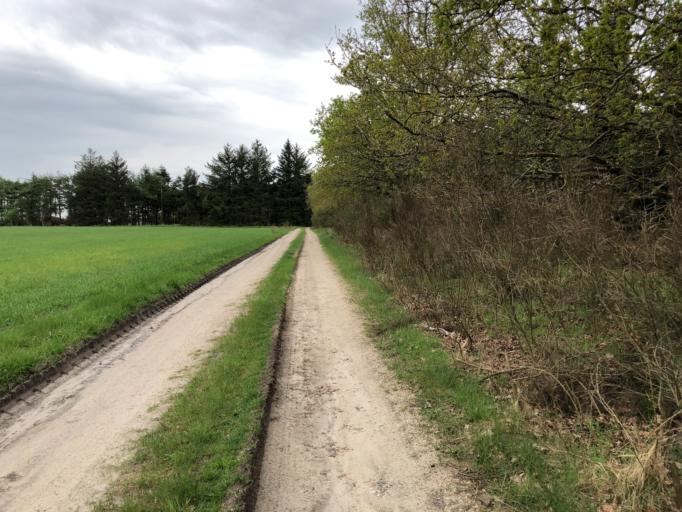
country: DK
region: Central Jutland
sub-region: Holstebro Kommune
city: Ulfborg
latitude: 56.2958
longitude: 8.4226
